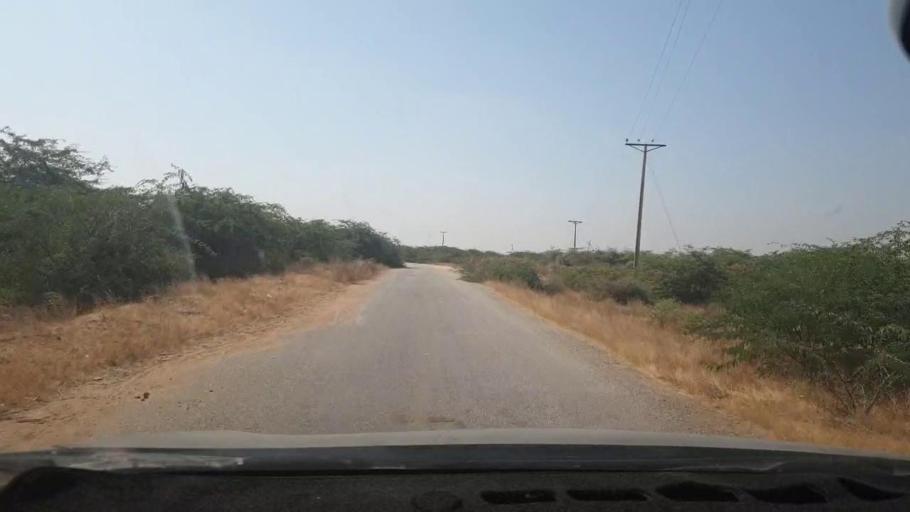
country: PK
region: Sindh
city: Malir Cantonment
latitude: 25.1543
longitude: 67.1359
